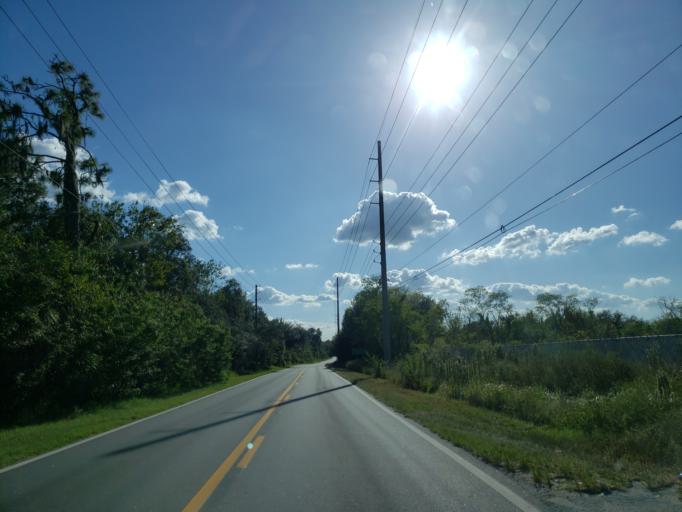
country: US
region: Florida
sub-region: Hillsborough County
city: Dover
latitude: 27.9887
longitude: -82.1663
